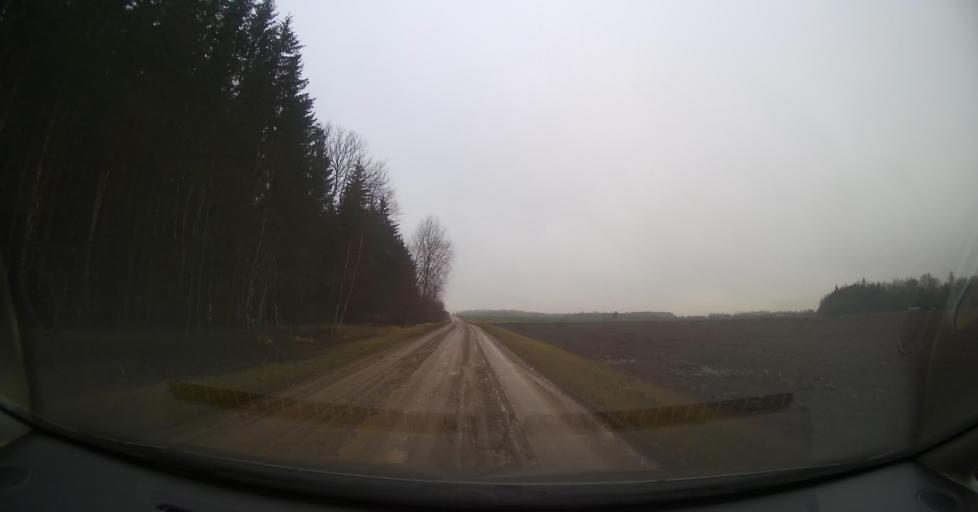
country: EE
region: Tartu
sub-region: Tartu linn
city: Tartu
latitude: 58.3976
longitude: 26.9190
